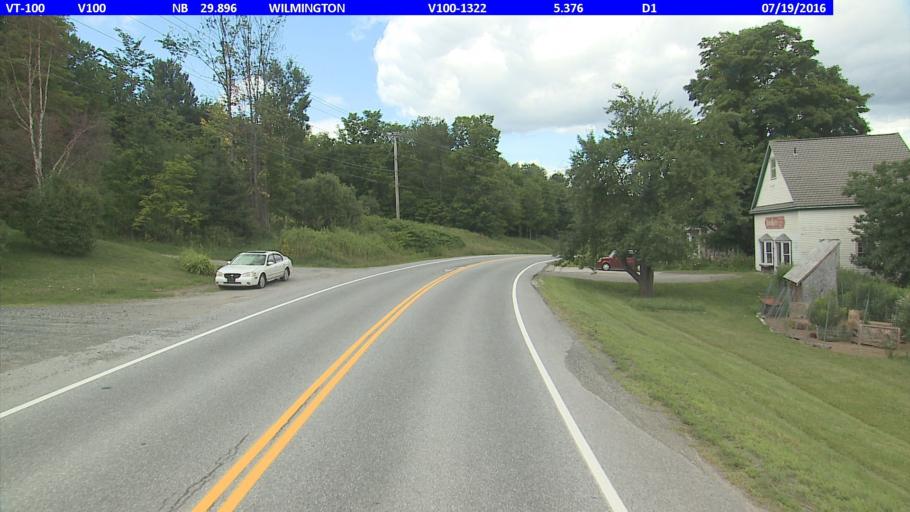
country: US
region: Vermont
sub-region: Windham County
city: Dover
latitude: 42.9036
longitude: -72.8530
